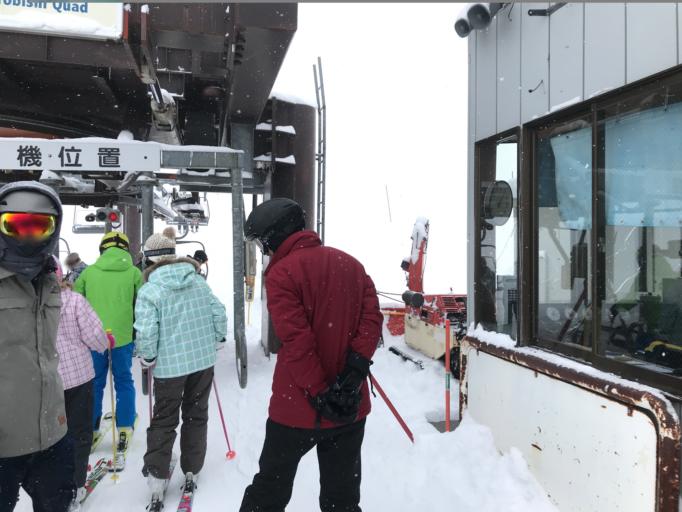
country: JP
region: Nagano
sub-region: Kitaazumi Gun
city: Hakuba
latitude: 36.7011
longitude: 137.8105
